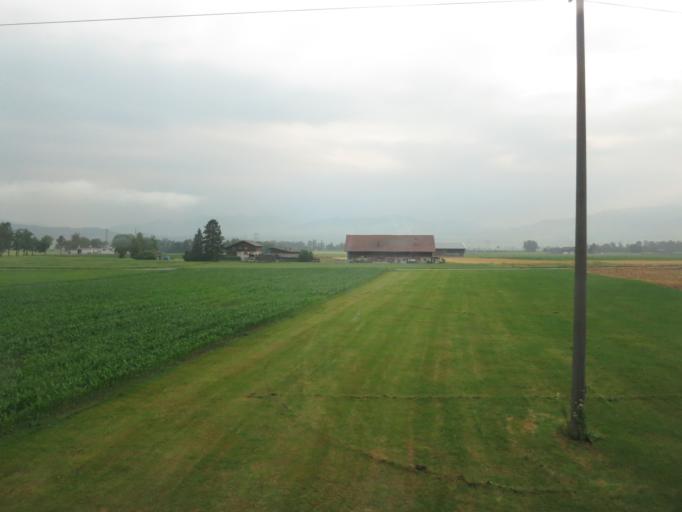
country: CH
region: Schwyz
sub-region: Bezirk March
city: Reichenburg
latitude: 47.1758
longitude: 8.9641
